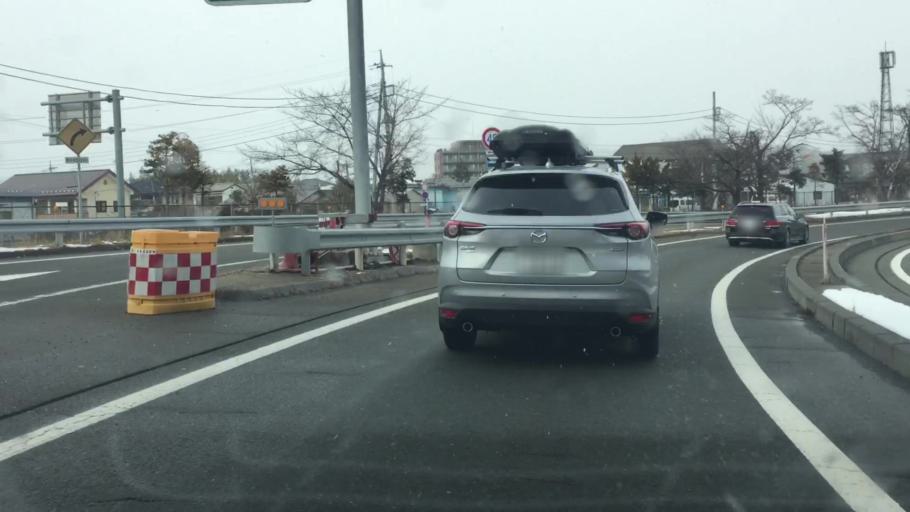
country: JP
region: Gunma
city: Numata
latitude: 36.6560
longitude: 139.0688
